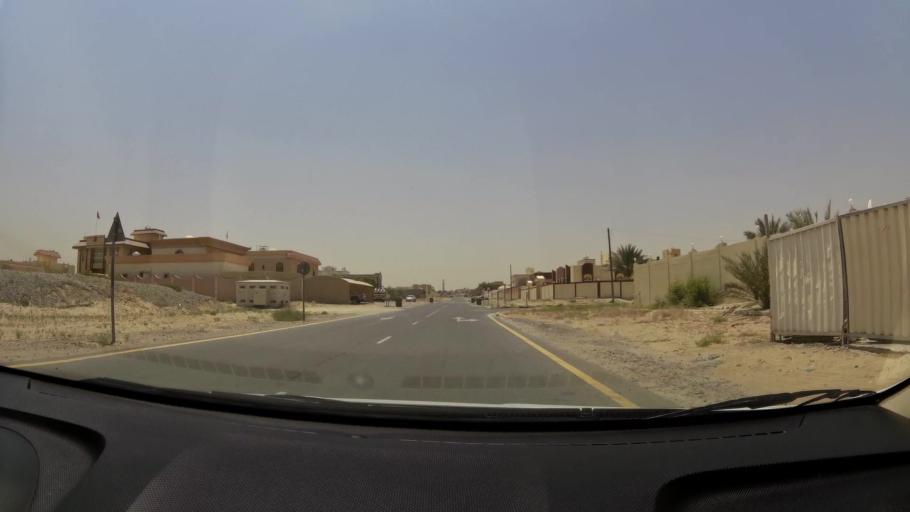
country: AE
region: Ajman
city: Ajman
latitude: 25.4086
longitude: 55.5190
